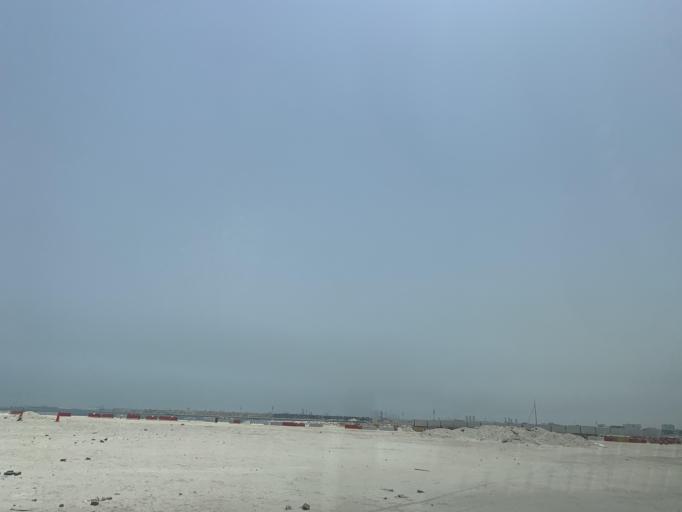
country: BH
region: Muharraq
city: Al Hadd
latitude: 26.2548
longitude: 50.6664
